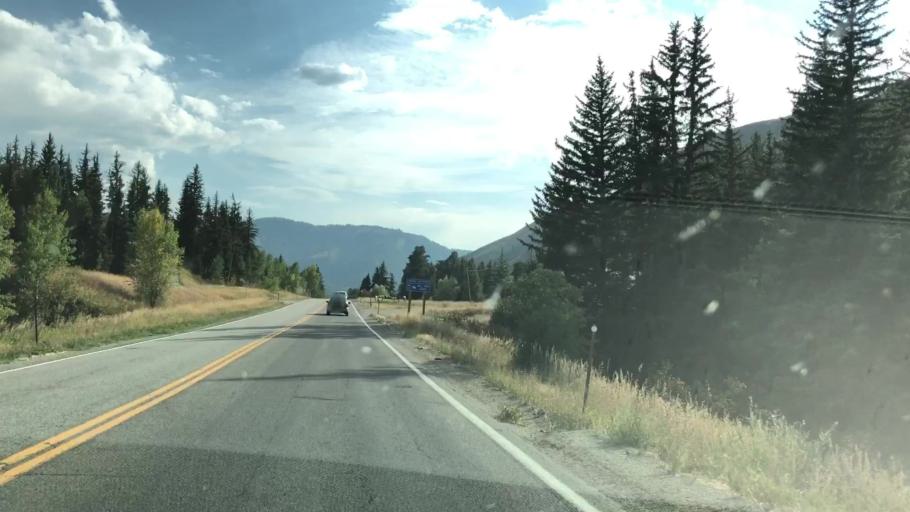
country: US
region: Wyoming
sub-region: Teton County
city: Hoback
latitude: 43.3402
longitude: -110.7232
